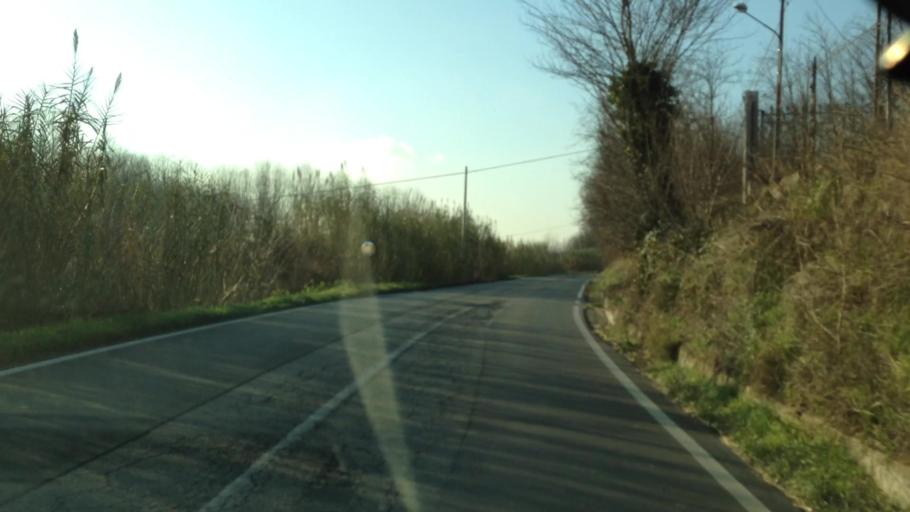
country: IT
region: Piedmont
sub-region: Provincia di Asti
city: Cortiglione
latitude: 44.8311
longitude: 8.3644
